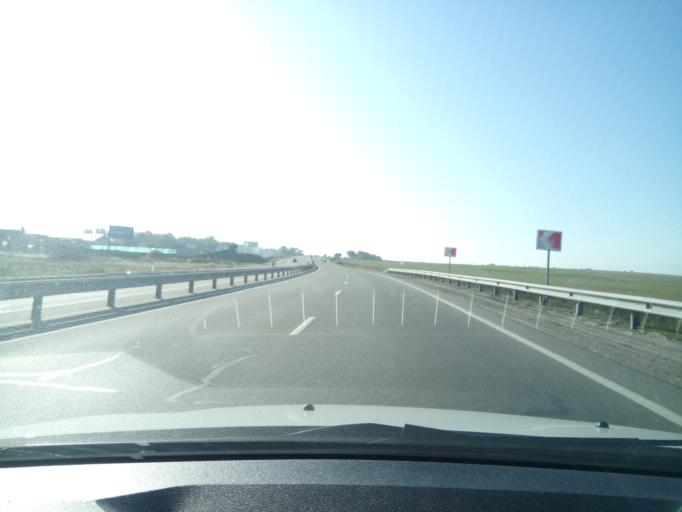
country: RU
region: Nizjnij Novgorod
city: Burevestnik
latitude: 56.1491
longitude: 43.9084
